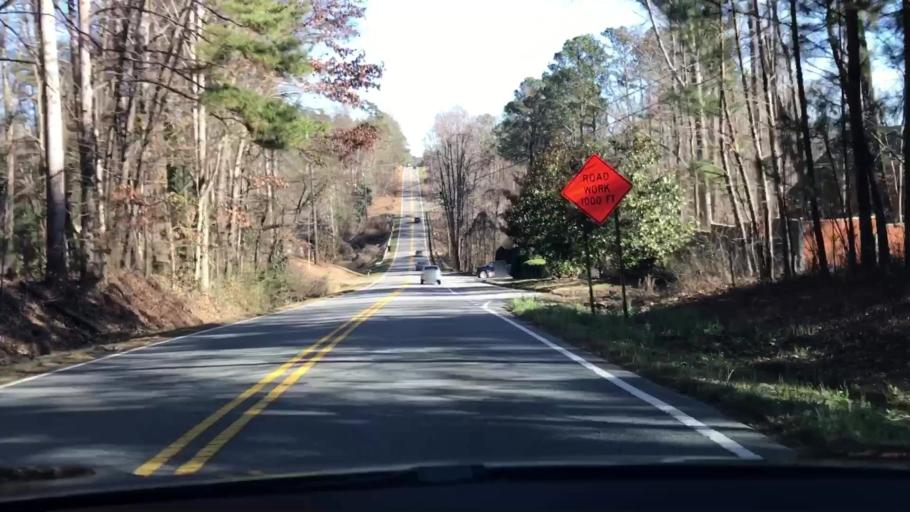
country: US
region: Georgia
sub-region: Forsyth County
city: Cumming
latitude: 34.1836
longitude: -84.1025
